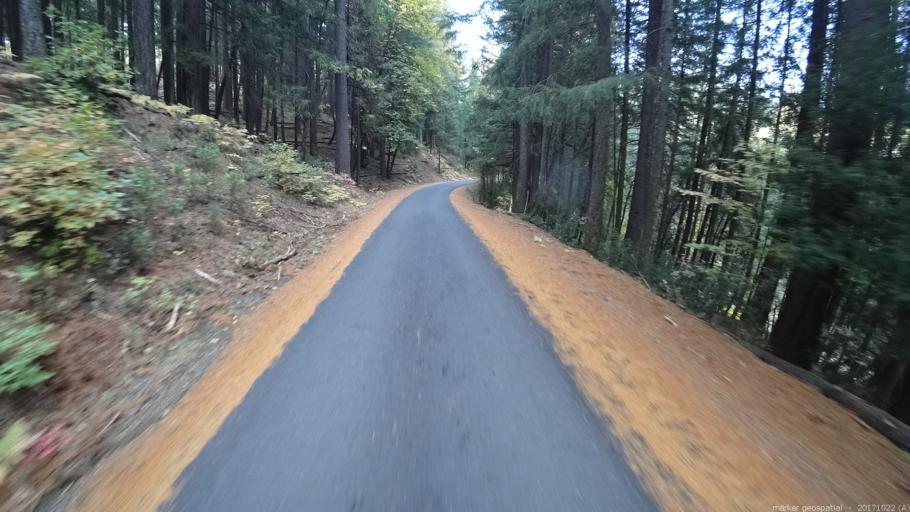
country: US
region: California
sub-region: Siskiyou County
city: Dunsmuir
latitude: 41.1542
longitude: -122.2895
